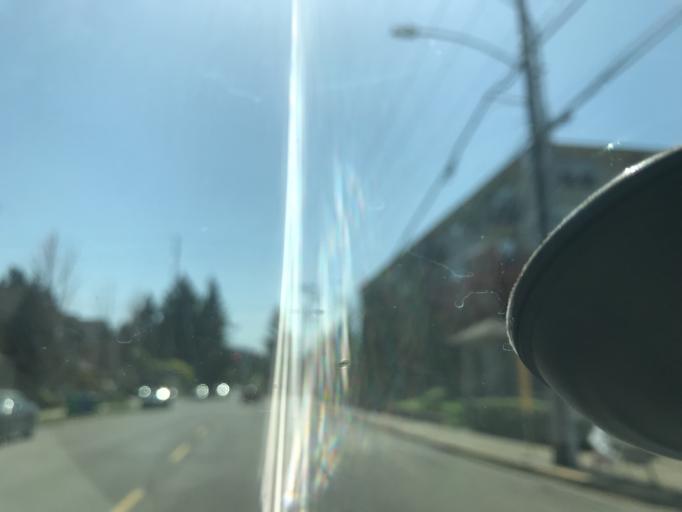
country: US
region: Oregon
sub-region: Multnomah County
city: Lents
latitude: 45.4906
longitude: -122.5558
